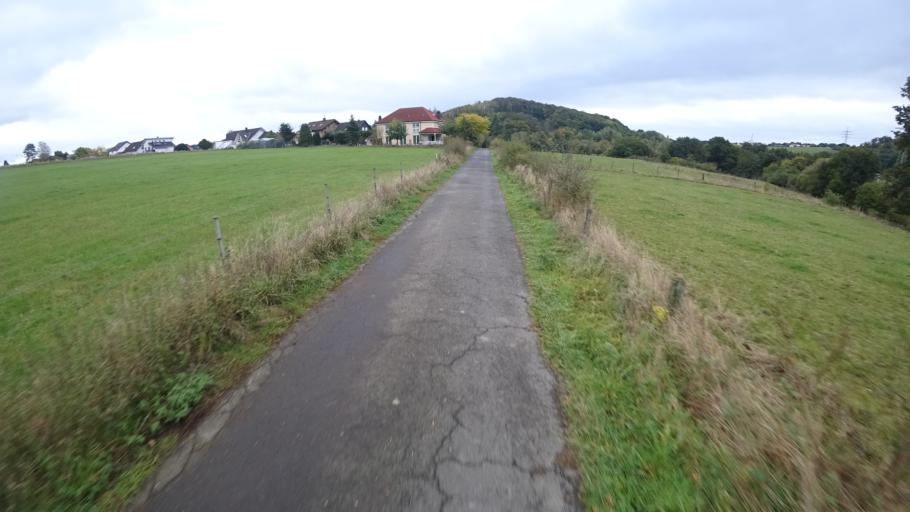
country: DE
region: Rheinland-Pfalz
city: Nordhofen
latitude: 50.5249
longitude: 7.7404
